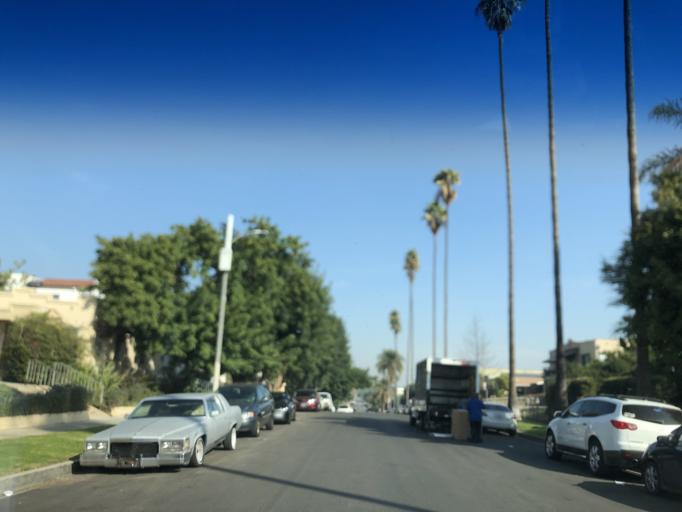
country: US
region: California
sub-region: Los Angeles County
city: Hollywood
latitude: 34.0498
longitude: -118.3243
